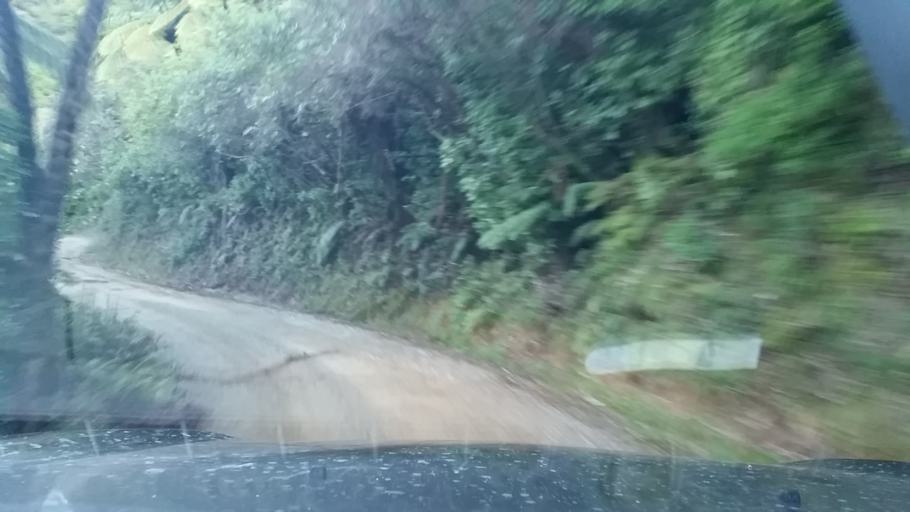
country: NZ
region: Marlborough
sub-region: Marlborough District
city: Picton
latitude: -41.1314
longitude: 174.1486
